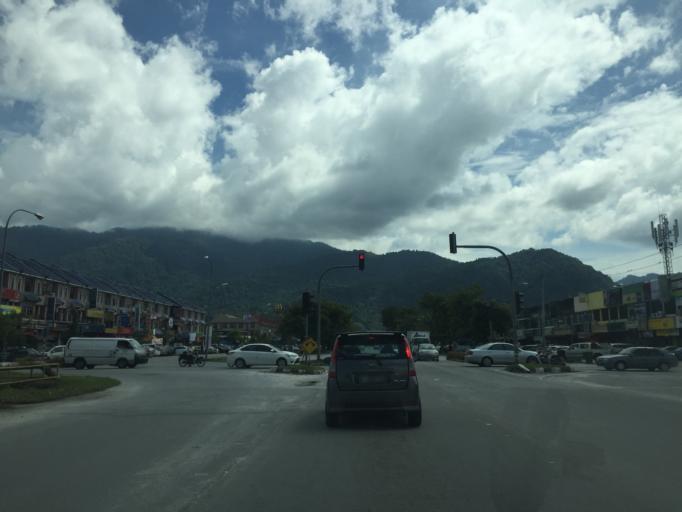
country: MY
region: Perak
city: Kampar
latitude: 4.3262
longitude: 101.1425
